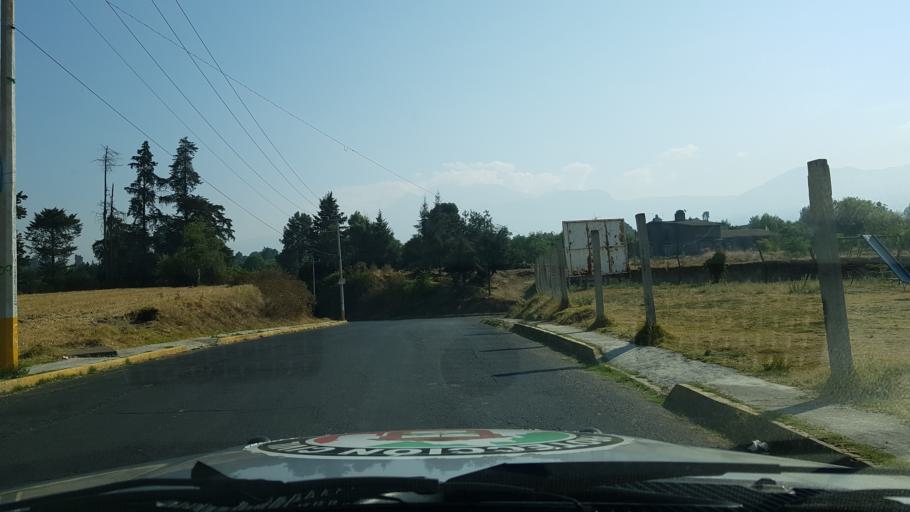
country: MX
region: Mexico
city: Atlautla
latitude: 19.0379
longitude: -98.7746
